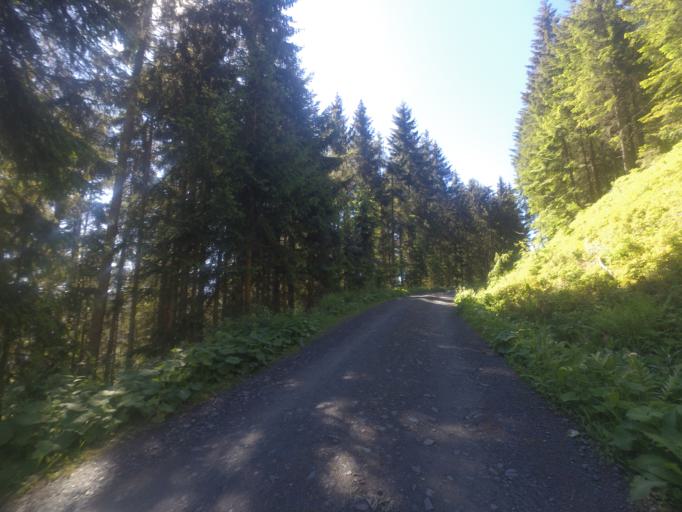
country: AT
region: Salzburg
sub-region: Politischer Bezirk Zell am See
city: Lend
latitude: 47.3253
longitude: 13.0518
